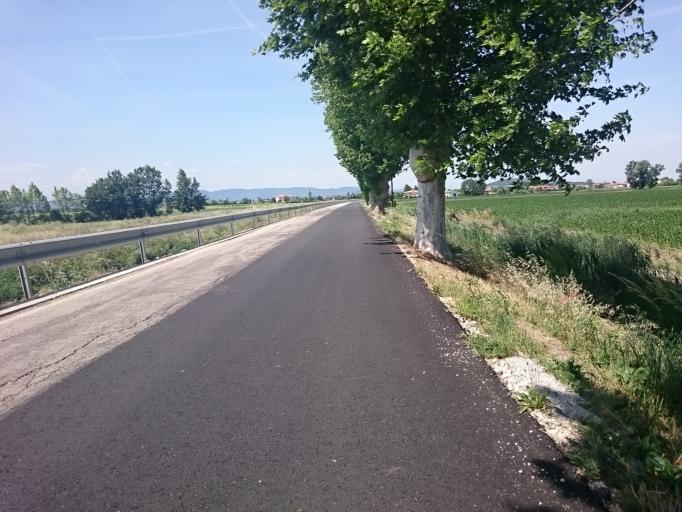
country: IT
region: Veneto
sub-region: Provincia di Padova
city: Lozzo Atestino
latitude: 45.3040
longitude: 11.6035
